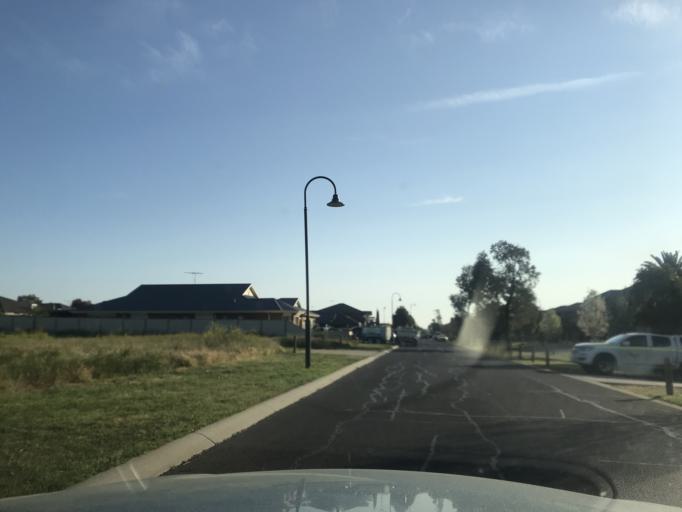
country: AU
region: Victoria
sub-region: Wyndham
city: Williams Landing
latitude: -37.8607
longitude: 144.7266
